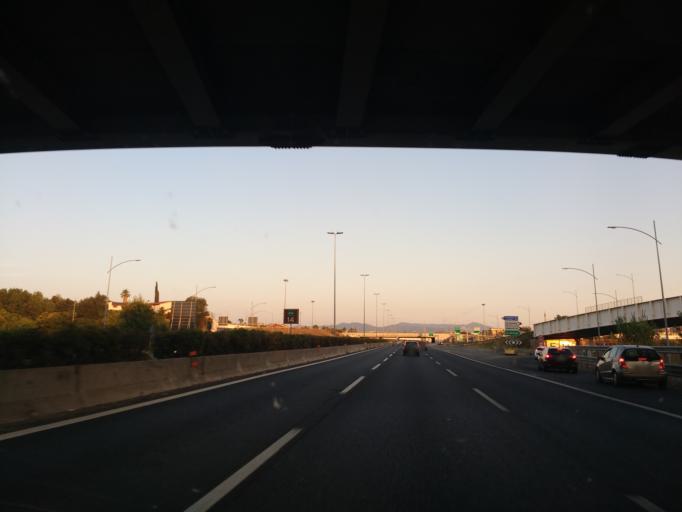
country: IT
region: Latium
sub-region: Citta metropolitana di Roma Capitale
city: Setteville
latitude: 41.9237
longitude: 12.6088
